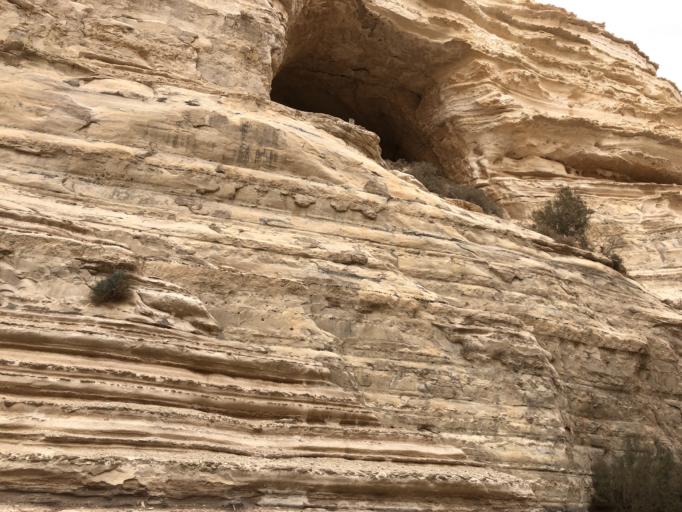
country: IL
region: Southern District
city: Midreshet Ben-Gurion
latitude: 30.8270
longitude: 34.7647
